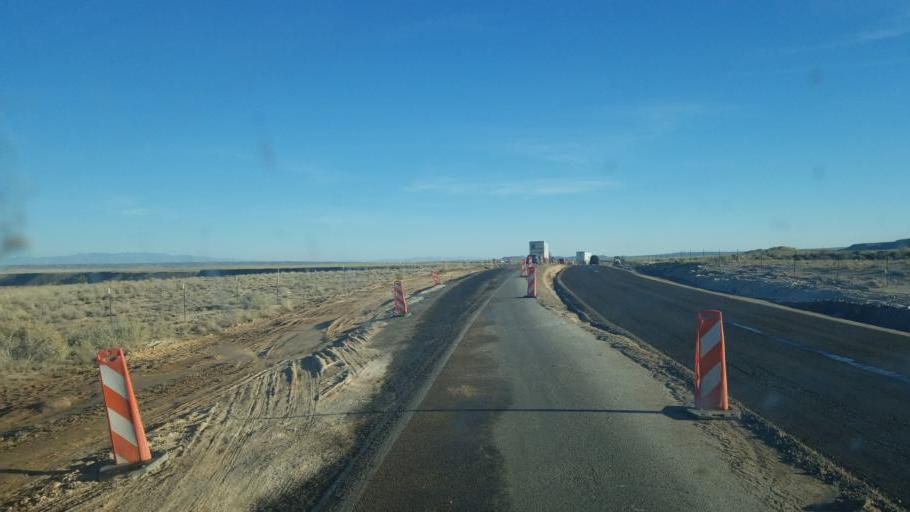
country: US
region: New Mexico
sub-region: Cibola County
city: Laguna
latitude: 34.9032
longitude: -107.0888
